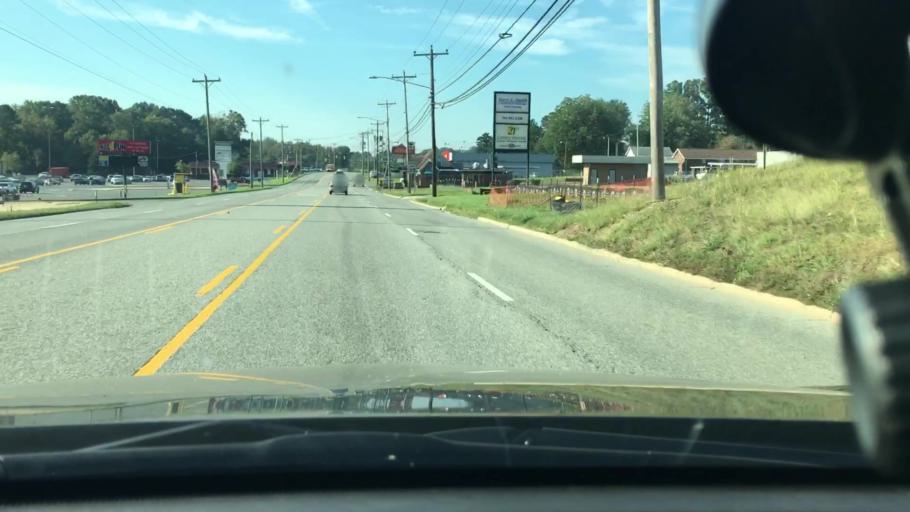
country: US
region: North Carolina
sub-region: Stanly County
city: Albemarle
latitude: 35.3749
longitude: -80.1965
